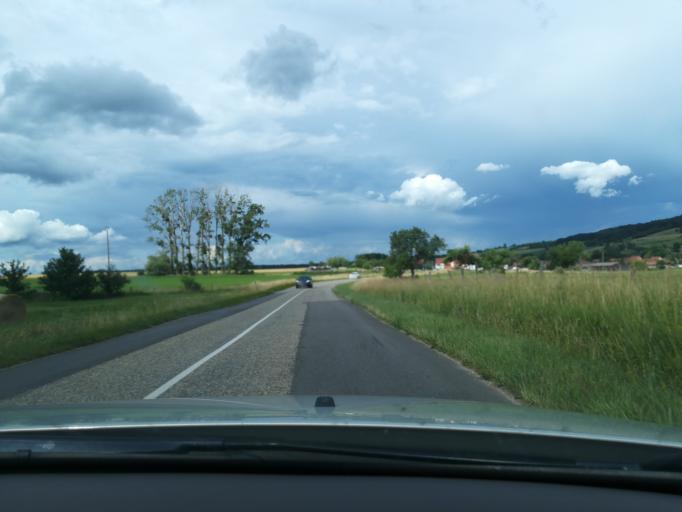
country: FR
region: Alsace
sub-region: Departement du Bas-Rhin
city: Neuwiller-les-Saverne
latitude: 48.8128
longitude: 7.4275
